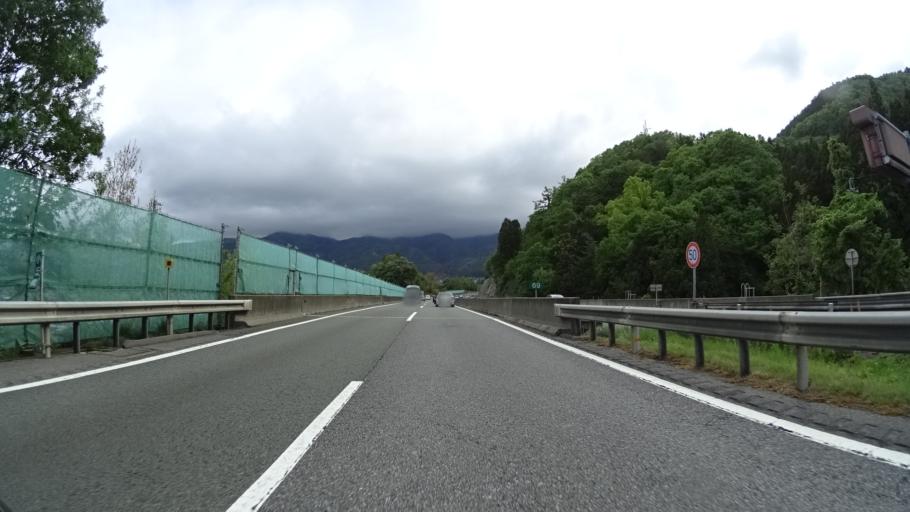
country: JP
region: Nagano
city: Nagano-shi
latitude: 36.5323
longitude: 138.0870
